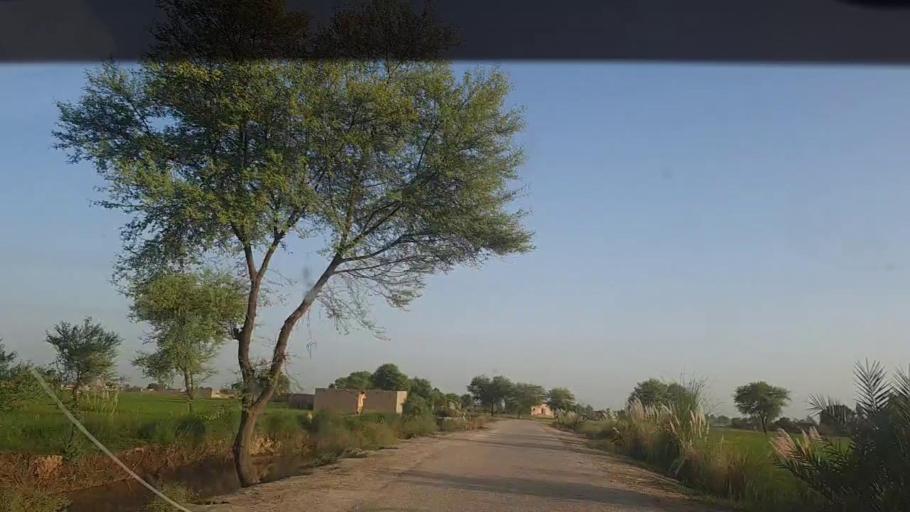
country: PK
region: Sindh
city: Thul
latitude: 28.1215
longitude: 68.8952
